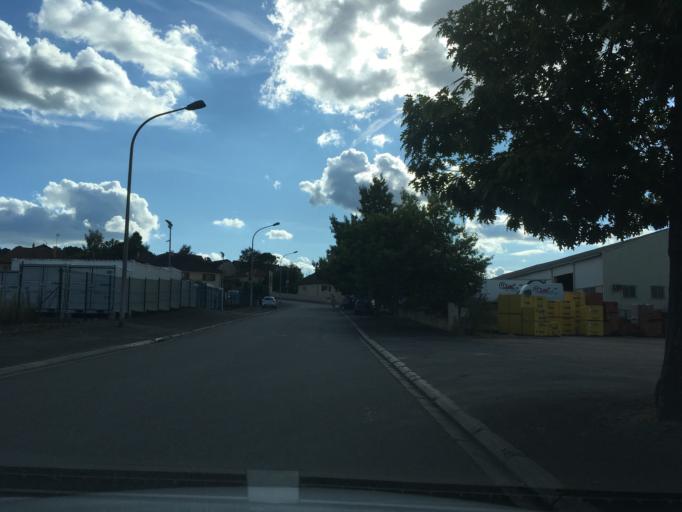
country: FR
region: Limousin
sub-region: Departement de la Correze
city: Malemort-sur-Correze
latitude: 45.1513
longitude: 1.5649
